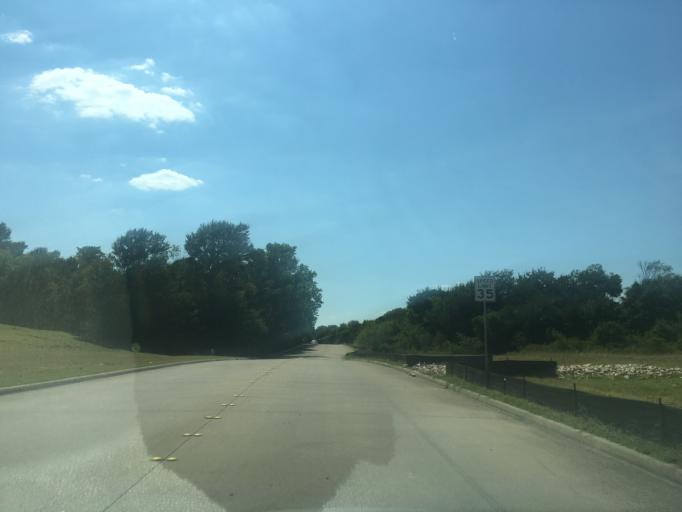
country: US
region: Texas
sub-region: Denton County
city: Lewisville
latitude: 33.0093
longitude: -96.9825
